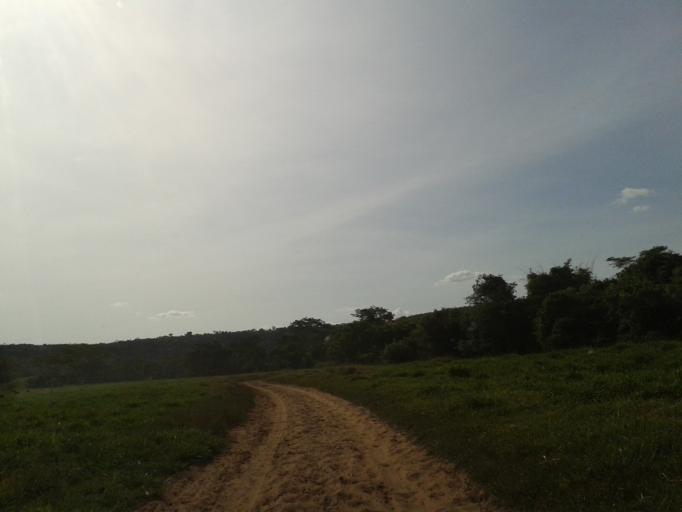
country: BR
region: Minas Gerais
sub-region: Campina Verde
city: Campina Verde
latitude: -19.4994
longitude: -49.5875
